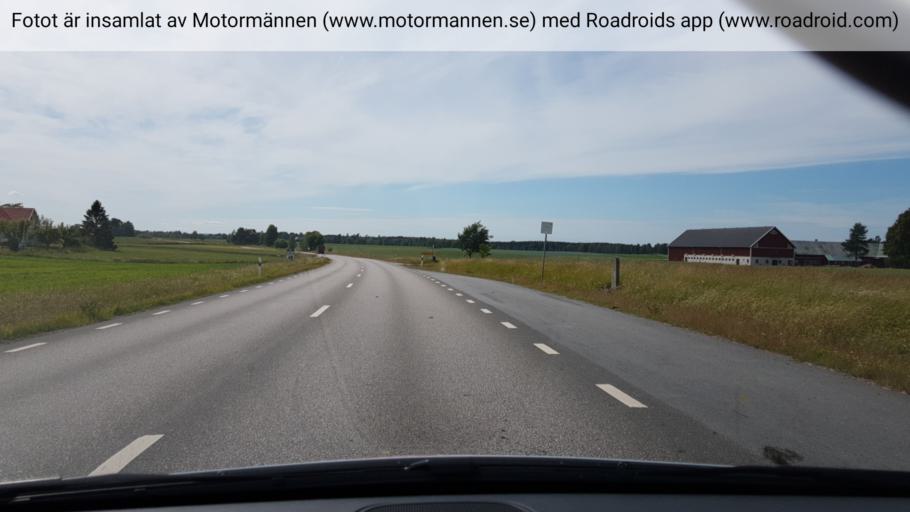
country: SE
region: Vaestra Goetaland
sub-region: Tibro Kommun
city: Tibro
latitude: 58.3467
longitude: 14.1439
